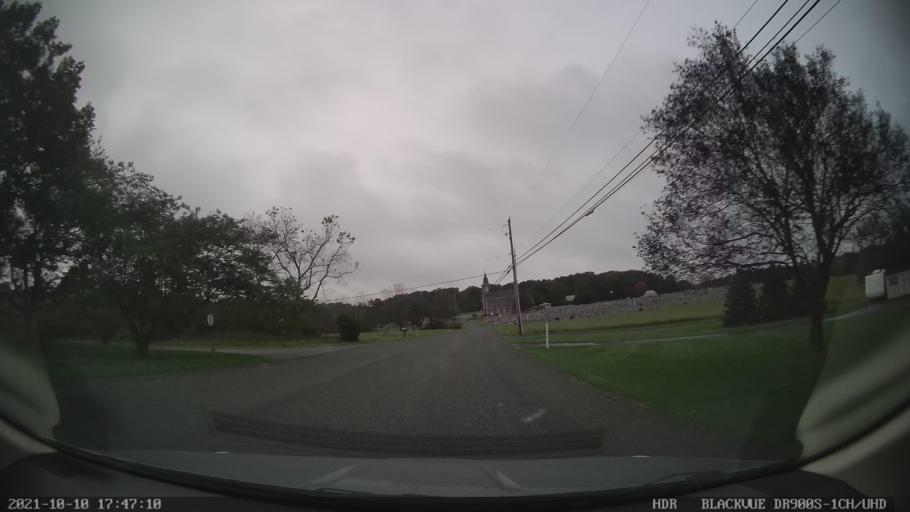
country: US
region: Pennsylvania
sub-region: Lehigh County
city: Breinigsville
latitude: 40.5718
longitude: -75.6790
